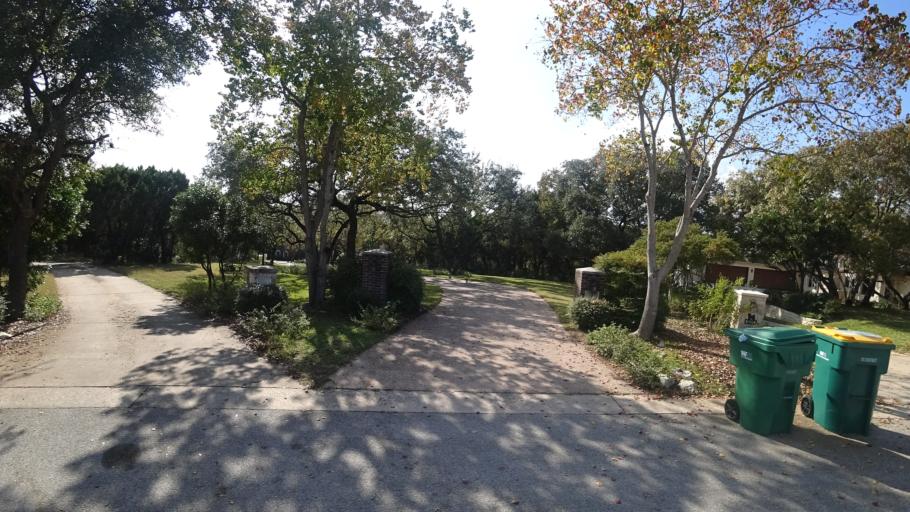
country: US
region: Texas
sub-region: Travis County
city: Lost Creek
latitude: 30.3013
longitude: -97.8509
